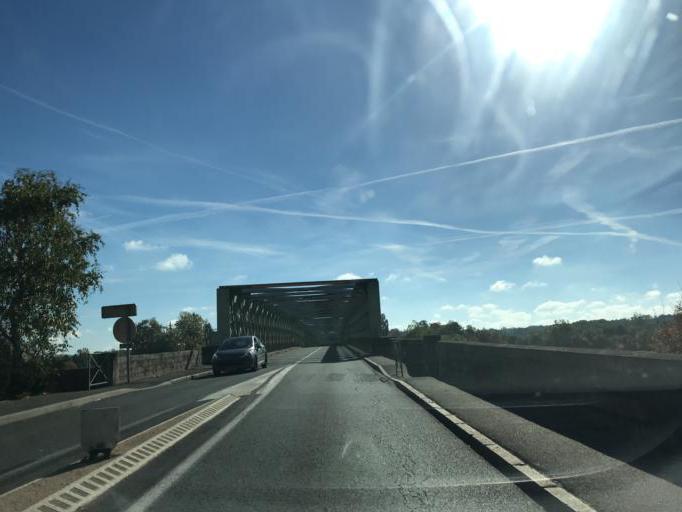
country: FR
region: Rhone-Alpes
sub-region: Departement du Rhone
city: Belleville
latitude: 46.1031
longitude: 4.7606
